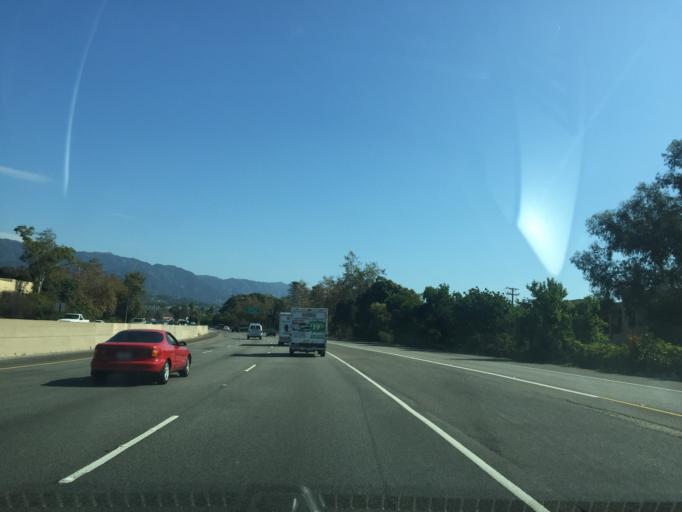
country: US
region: California
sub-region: Santa Barbara County
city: Santa Barbara
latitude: 34.4125
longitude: -119.6972
